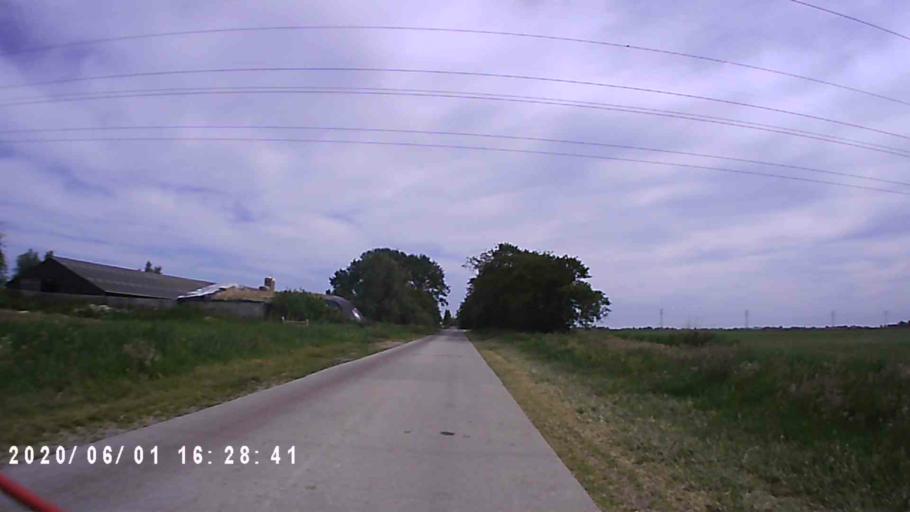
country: NL
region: Friesland
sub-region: Gemeente Leeuwarden
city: Camminghaburen
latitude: 53.1889
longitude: 5.8652
